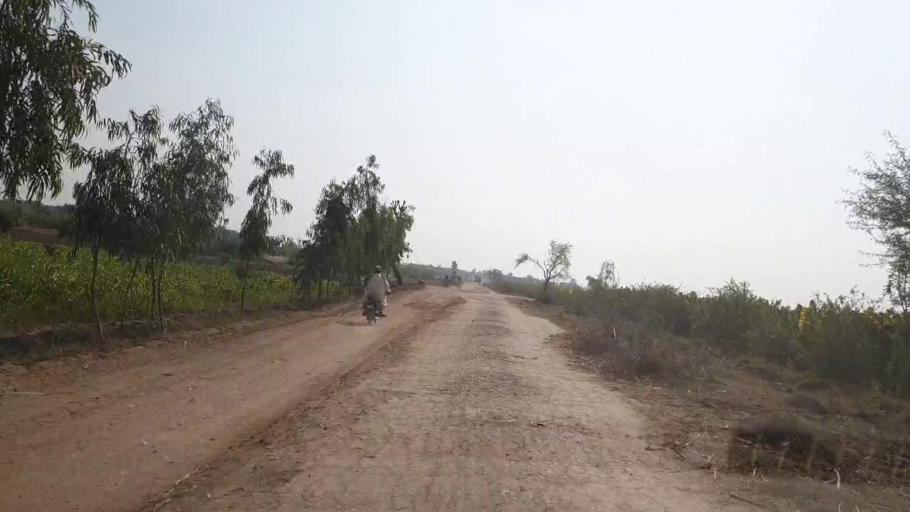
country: PK
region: Sindh
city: Bhit Shah
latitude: 25.7132
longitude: 68.5460
